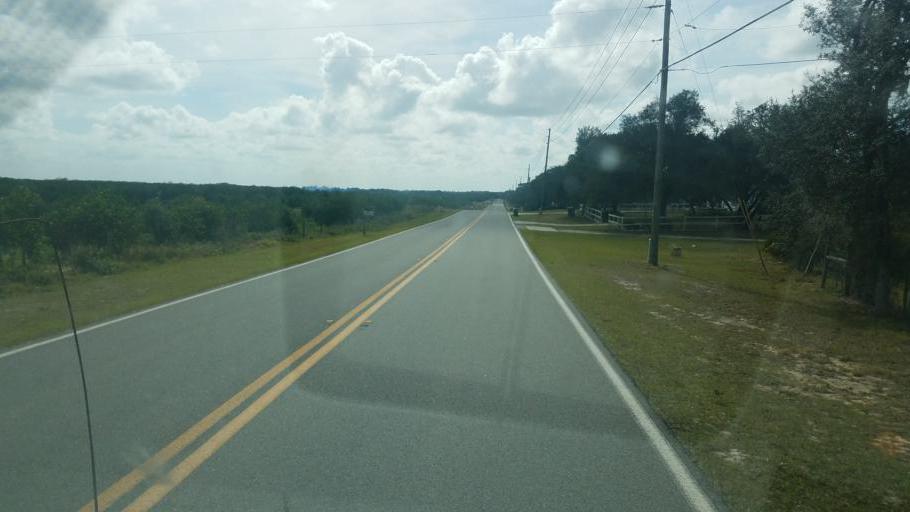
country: US
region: Florida
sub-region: Polk County
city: Dundee
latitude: 28.0313
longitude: -81.5292
